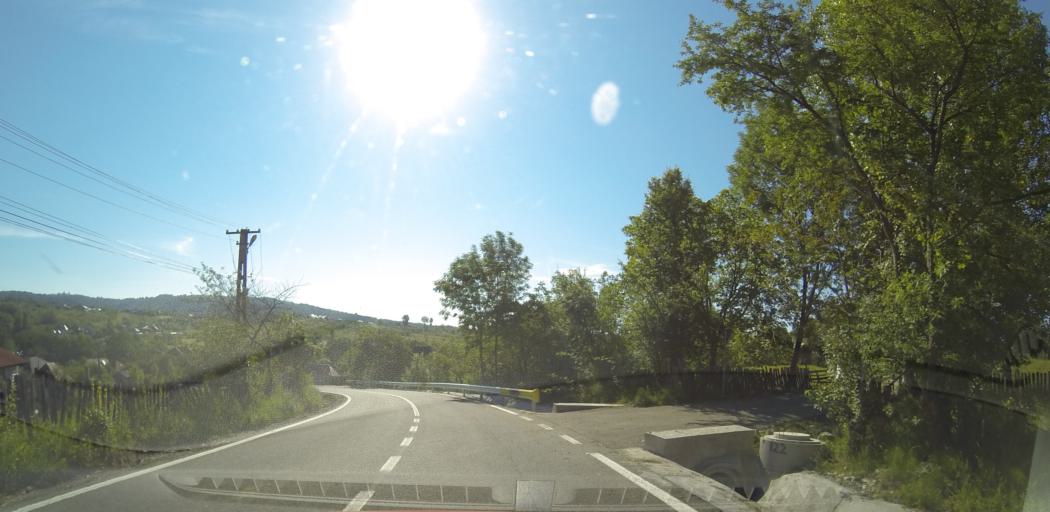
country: RO
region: Gorj
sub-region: Comuna Polovragi
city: Polovragi
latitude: 45.1726
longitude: 23.8645
